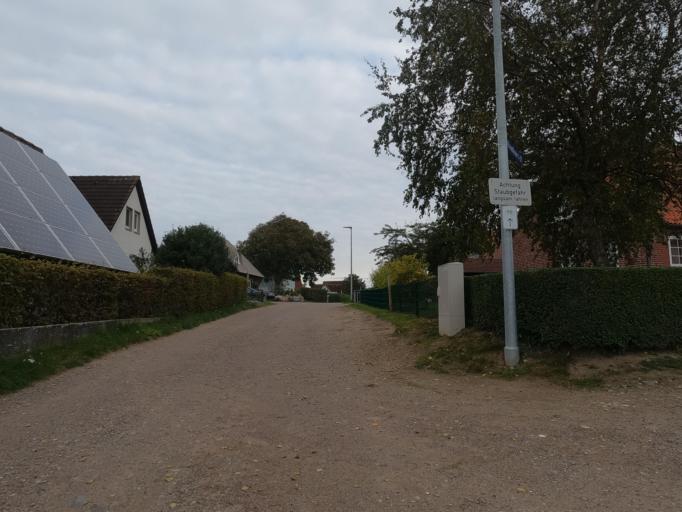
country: DE
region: Schleswig-Holstein
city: Heiligenhafen
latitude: 54.3673
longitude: 11.0206
